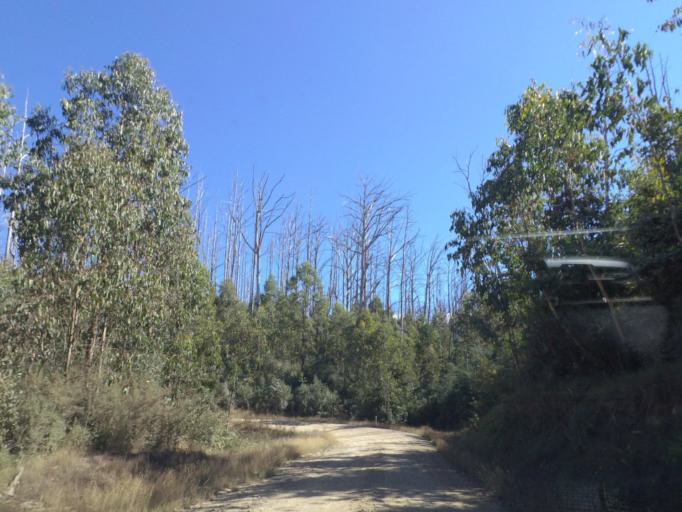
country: AU
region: Victoria
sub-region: Murrindindi
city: Alexandra
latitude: -37.4000
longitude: 145.8103
